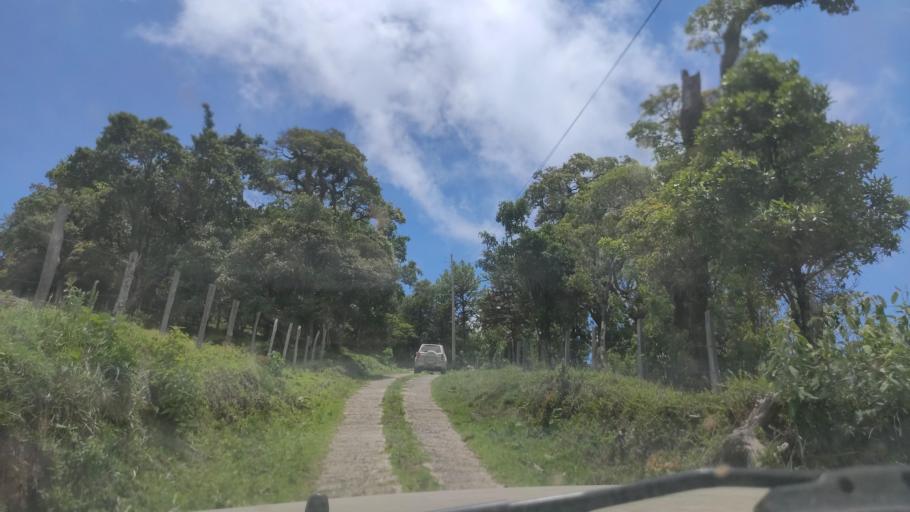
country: BR
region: Minas Gerais
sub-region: Cambui
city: Cambui
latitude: -22.6879
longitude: -45.9588
